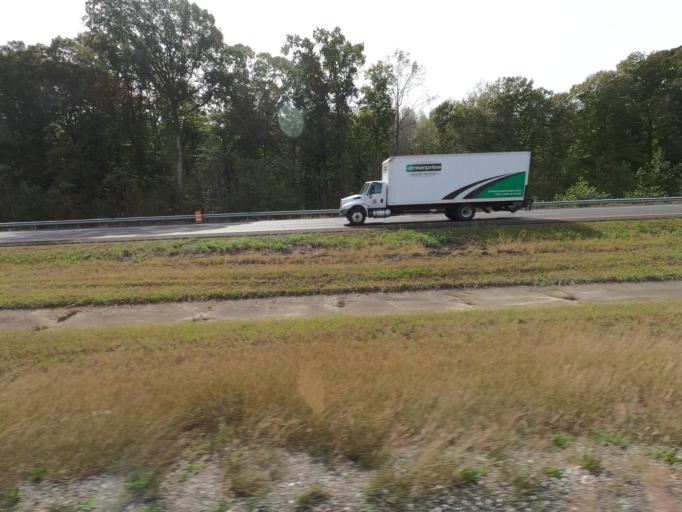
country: US
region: Tennessee
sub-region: Decatur County
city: Parsons
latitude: 35.8191
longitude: -88.1553
